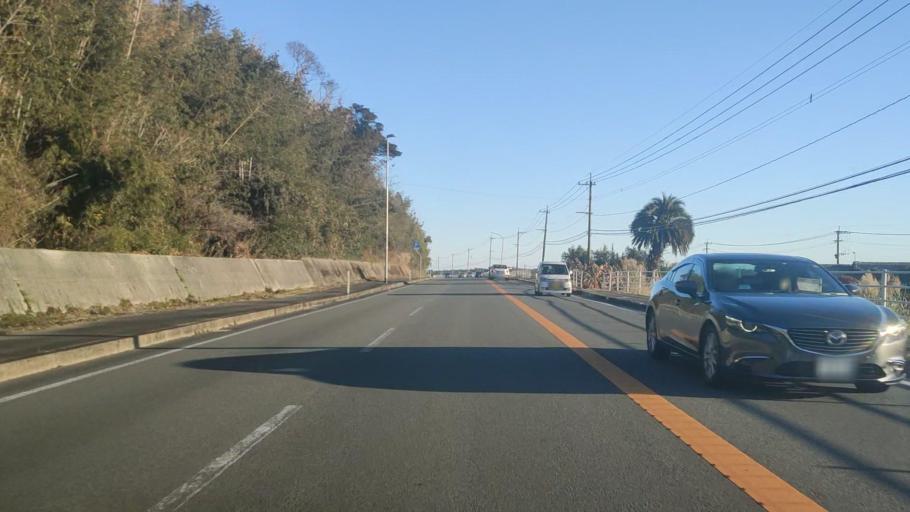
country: JP
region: Miyazaki
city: Takanabe
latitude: 32.1078
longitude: 131.5248
